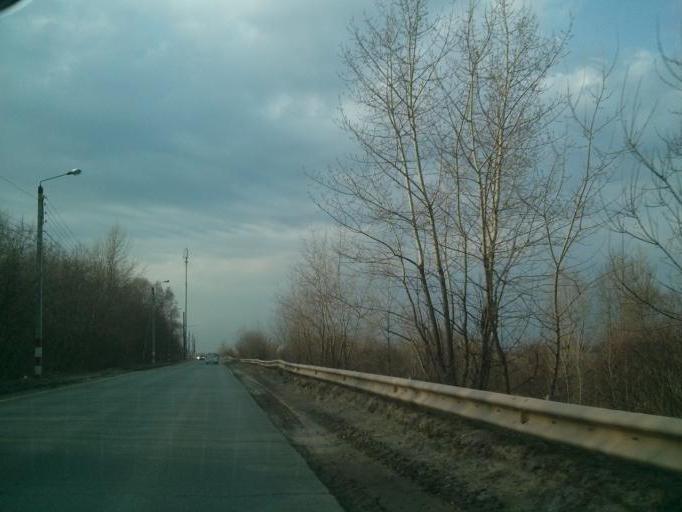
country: RU
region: Nizjnij Novgorod
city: Afonino
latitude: 56.3032
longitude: 44.0998
